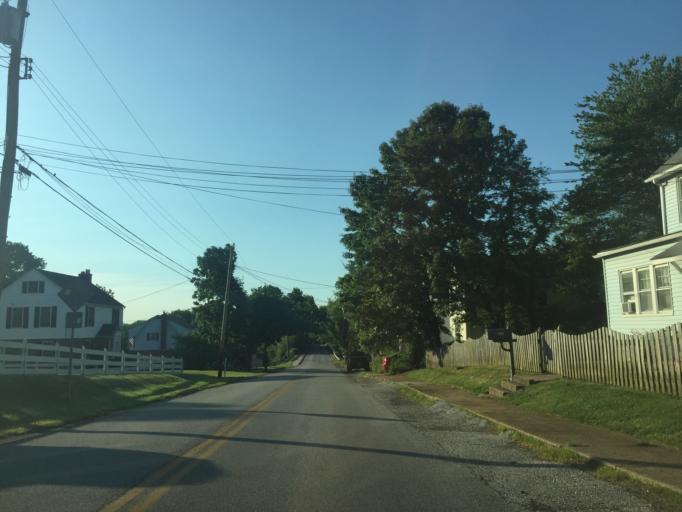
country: US
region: Maryland
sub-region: Howard County
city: Elkridge
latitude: 39.2254
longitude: -76.7073
